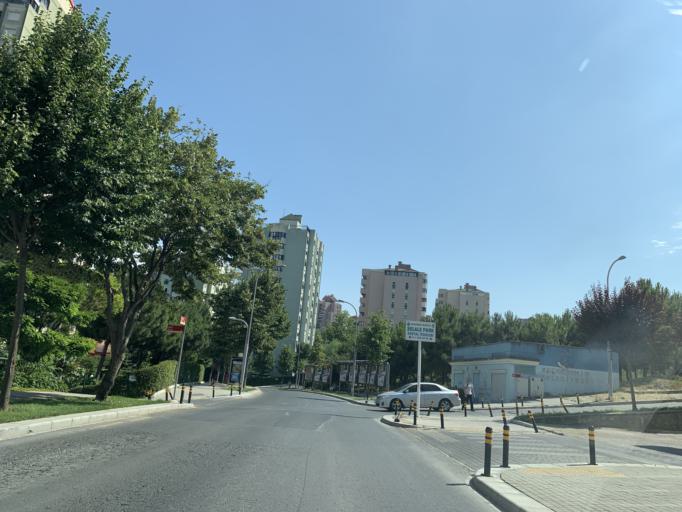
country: TR
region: Istanbul
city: Esenyurt
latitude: 41.0680
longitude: 28.6776
